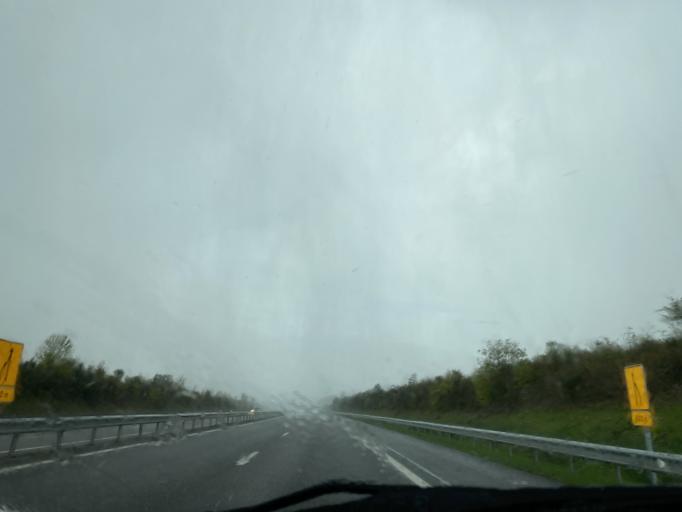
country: FR
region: Centre
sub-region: Departement du Cher
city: Trouy
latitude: 47.0367
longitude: 2.3649
